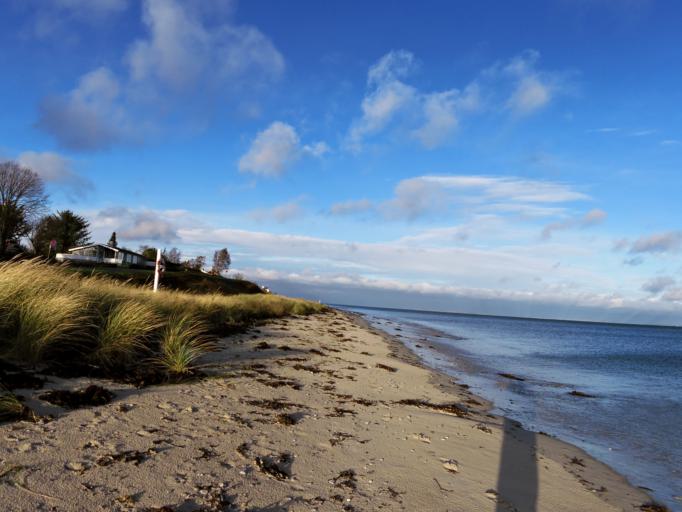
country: DK
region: Central Jutland
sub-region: Arhus Kommune
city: Beder
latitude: 56.0308
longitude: 10.2683
